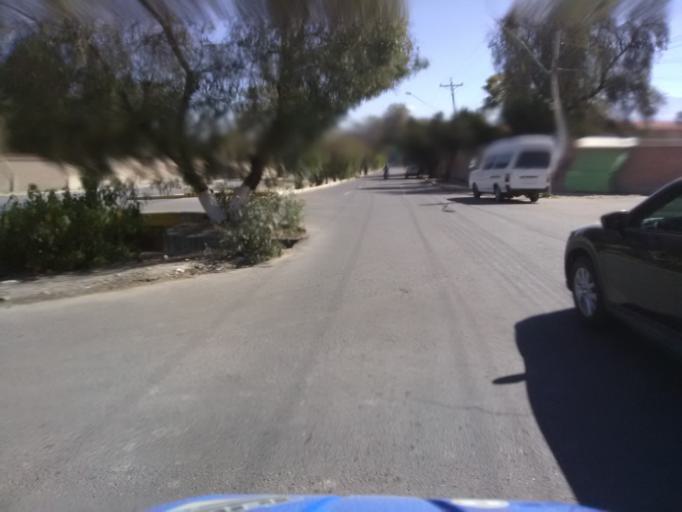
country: BO
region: Cochabamba
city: Cochabamba
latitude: -17.3815
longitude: -66.1961
